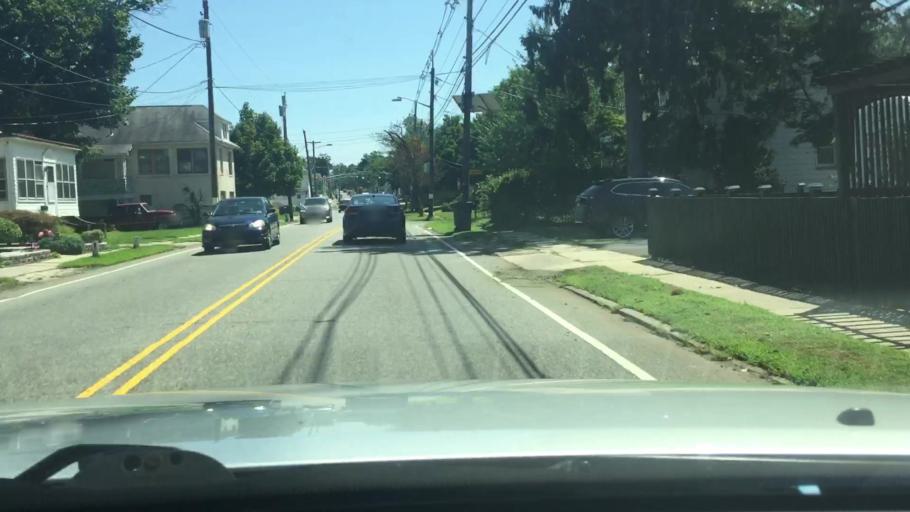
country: US
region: New Jersey
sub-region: Middlesex County
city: South River
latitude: 40.4428
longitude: -74.3921
